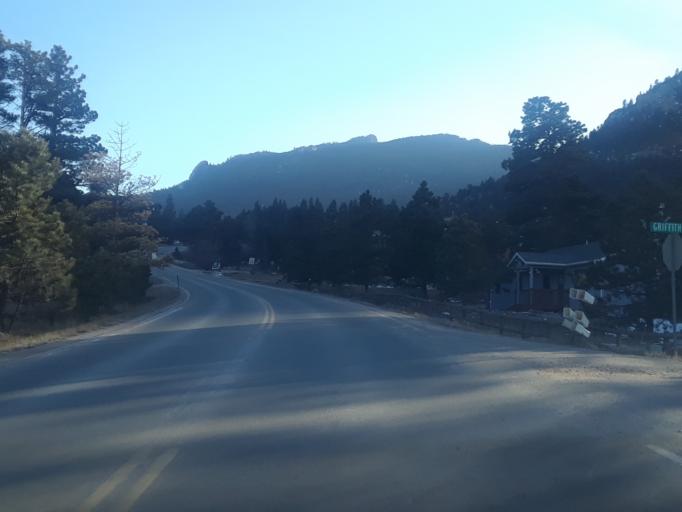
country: US
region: Colorado
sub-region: Larimer County
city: Estes Park
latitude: 40.3562
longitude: -105.5420
